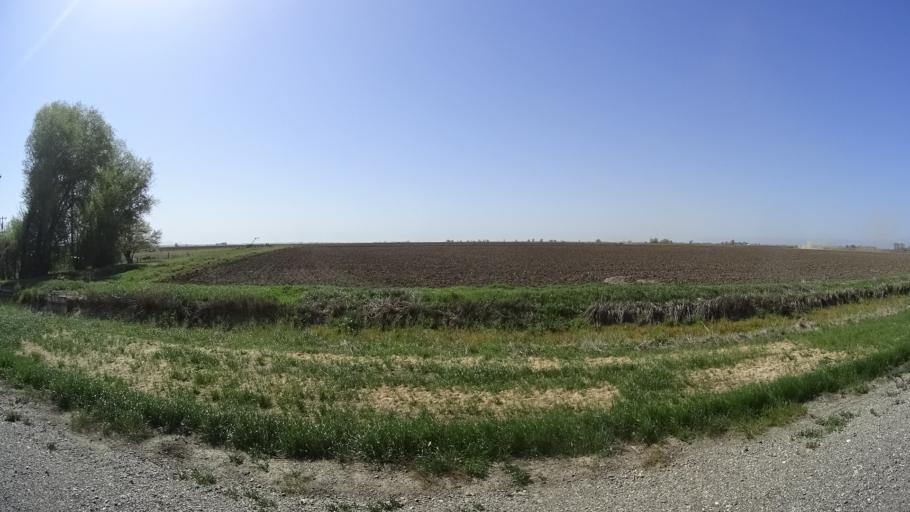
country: US
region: California
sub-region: Glenn County
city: Willows
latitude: 39.4578
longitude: -122.0757
